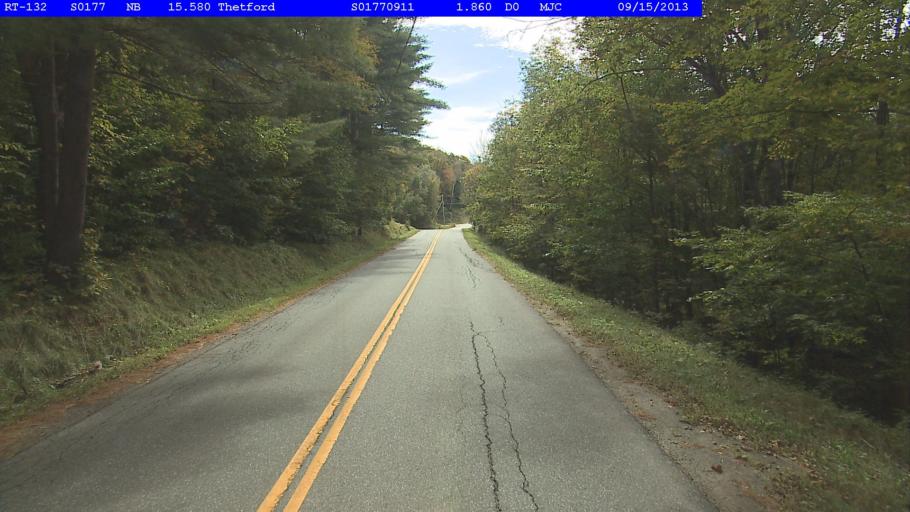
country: US
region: New Hampshire
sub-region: Grafton County
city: Hanover
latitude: 43.8281
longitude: -72.2878
